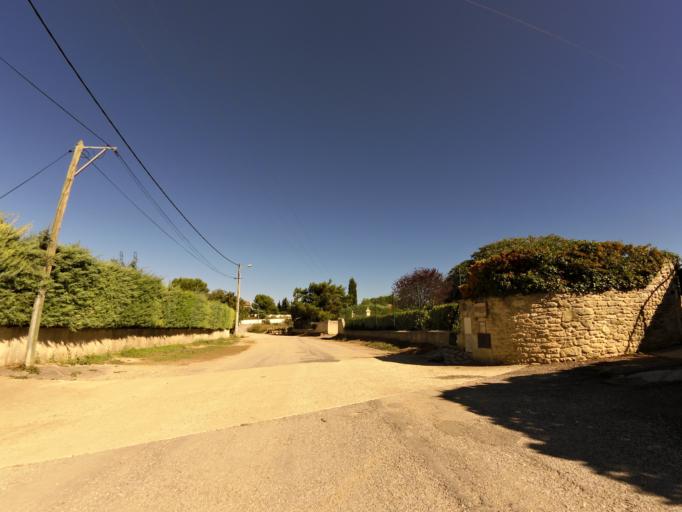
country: FR
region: Languedoc-Roussillon
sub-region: Departement du Gard
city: Aubais
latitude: 43.7439
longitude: 4.1418
